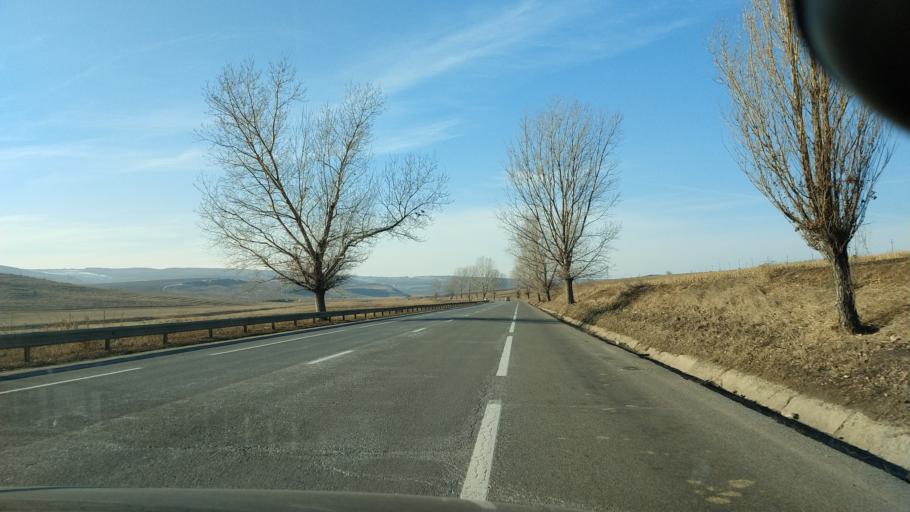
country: RO
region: Iasi
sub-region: Comuna Targu Frumos
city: Targu Frumos
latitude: 47.1975
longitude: 26.9853
